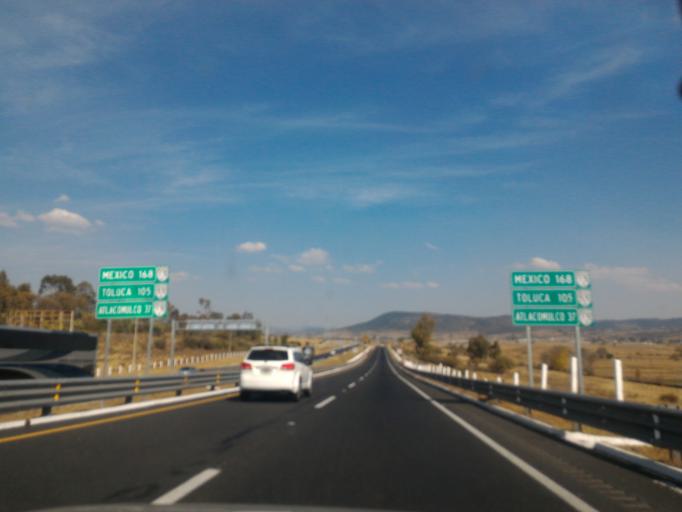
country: MX
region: Michoacan
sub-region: Contepec
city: El Cesped
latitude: 19.8771
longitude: -100.1732
